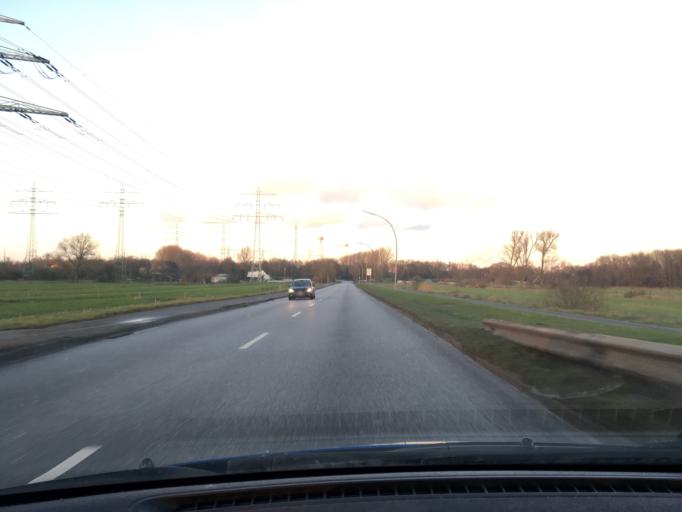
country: DE
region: Hamburg
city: Altona
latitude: 53.4911
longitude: 9.9077
